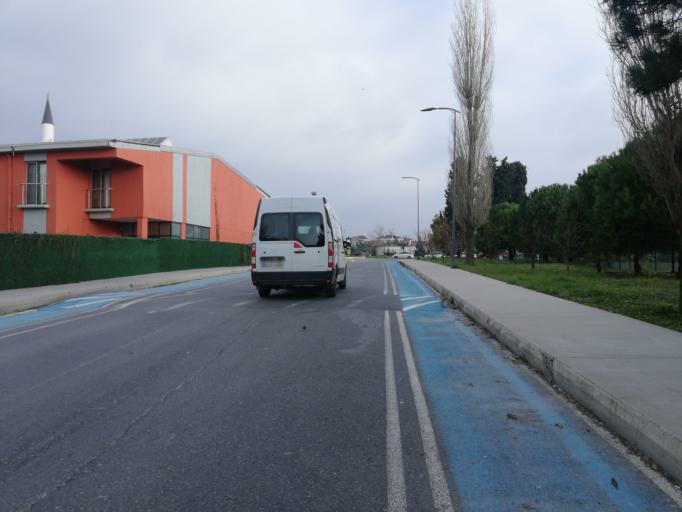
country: TR
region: Istanbul
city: merter keresteciler
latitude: 41.0279
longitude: 28.8878
